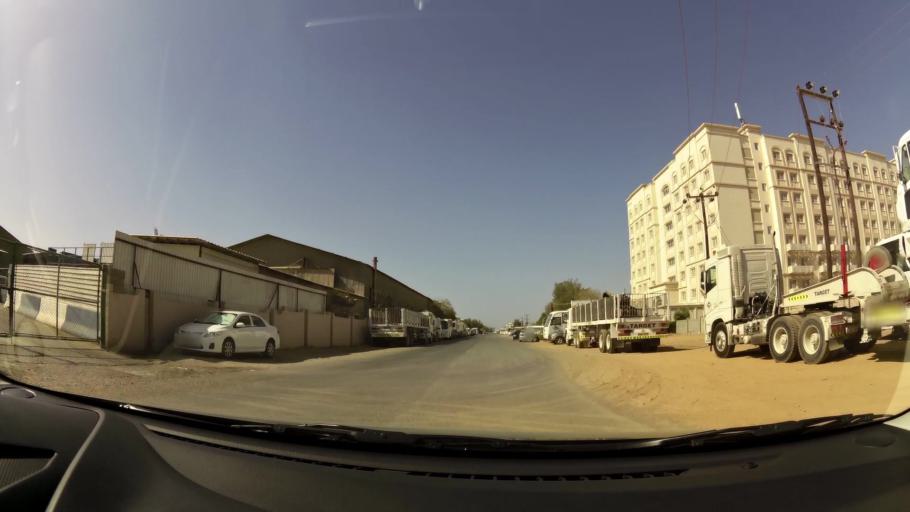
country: OM
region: Muhafazat Masqat
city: Bawshar
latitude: 23.5689
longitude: 58.3566
